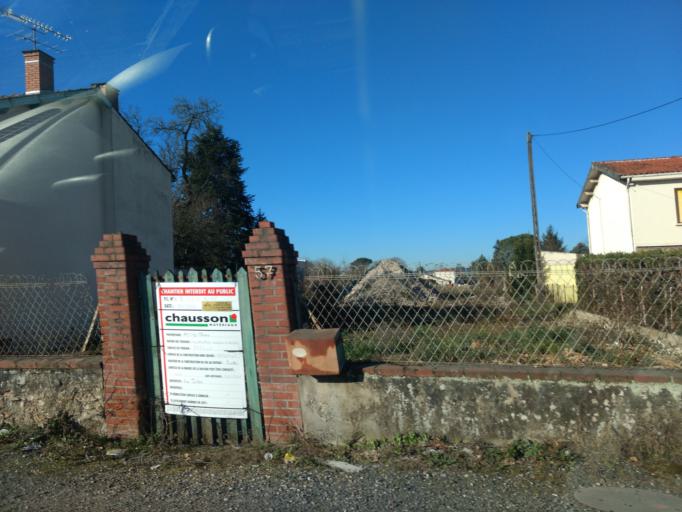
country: FR
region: Midi-Pyrenees
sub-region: Departement du Tarn
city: Albi
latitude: 43.9540
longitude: 2.1533
